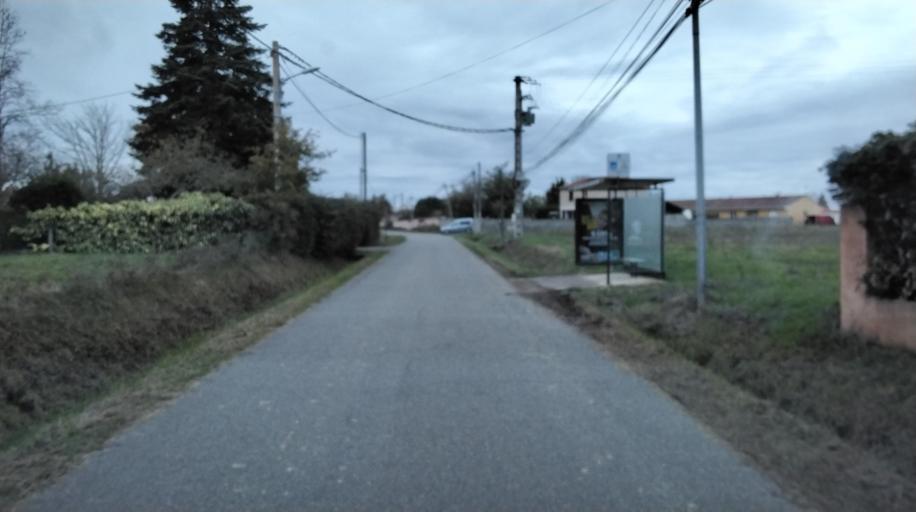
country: FR
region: Midi-Pyrenees
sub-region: Departement de la Haute-Garonne
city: Berat
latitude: 43.3891
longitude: 1.1923
